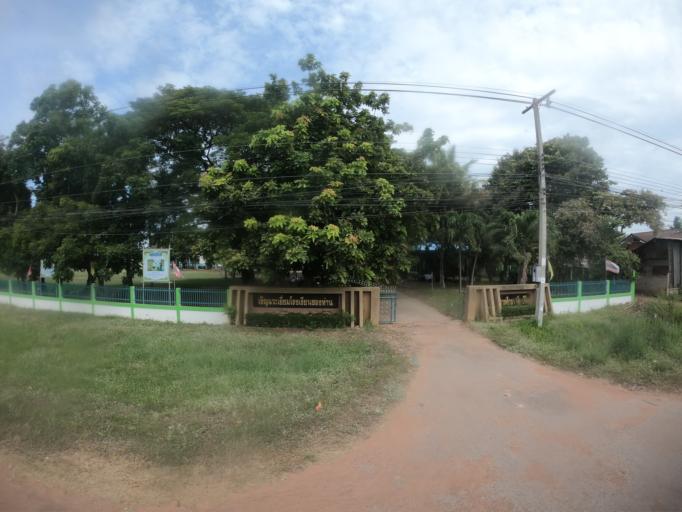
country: TH
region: Maha Sarakham
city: Chiang Yuen
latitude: 16.3449
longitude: 103.1262
